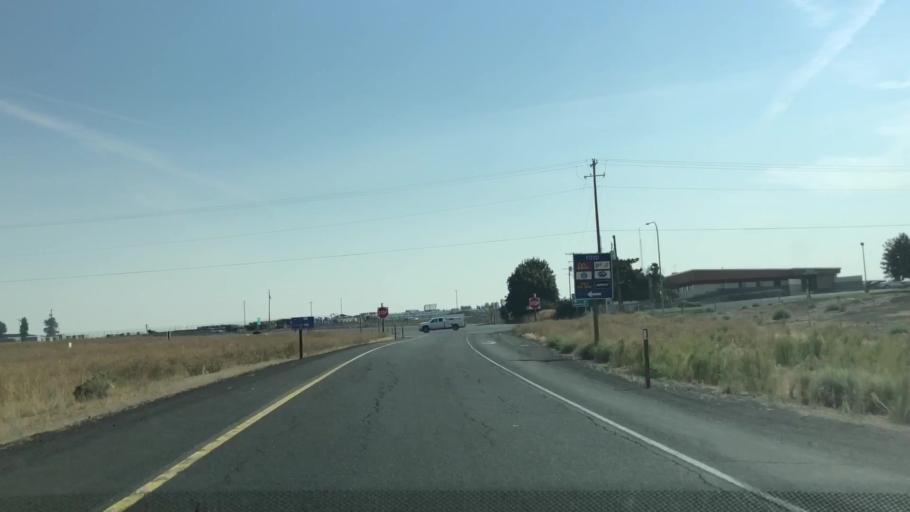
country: US
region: Washington
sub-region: Adams County
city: Ritzville
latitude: 47.1149
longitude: -118.3671
